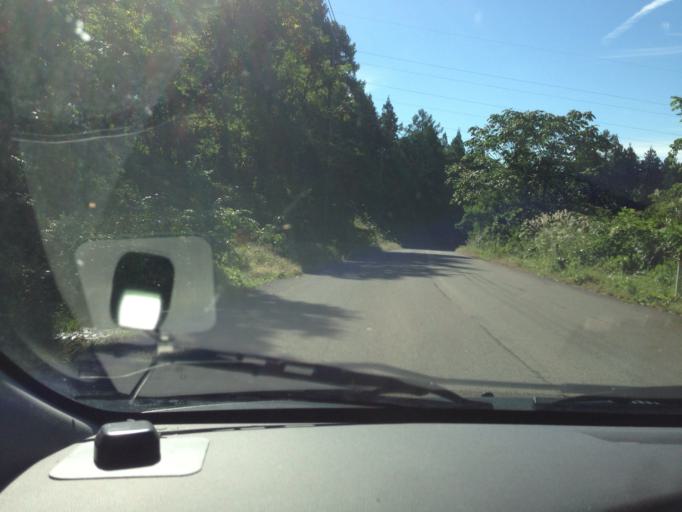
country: JP
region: Fukushima
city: Inawashiro
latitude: 37.5824
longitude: 140.1089
